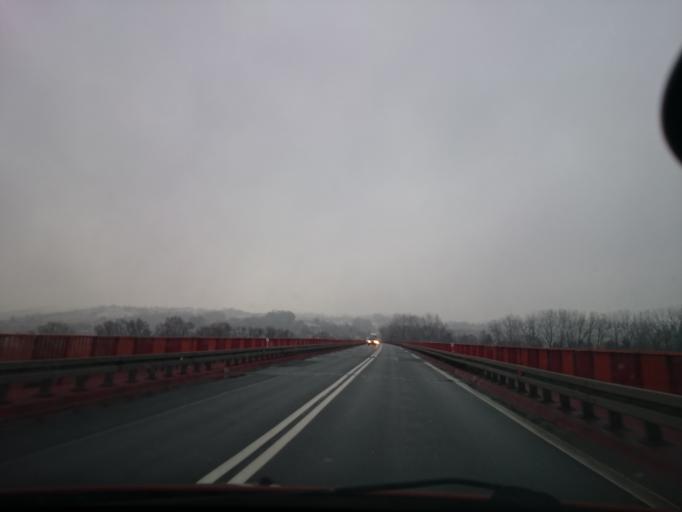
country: PL
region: Lower Silesian Voivodeship
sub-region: Powiat klodzki
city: Klodzko
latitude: 50.4572
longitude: 16.6547
